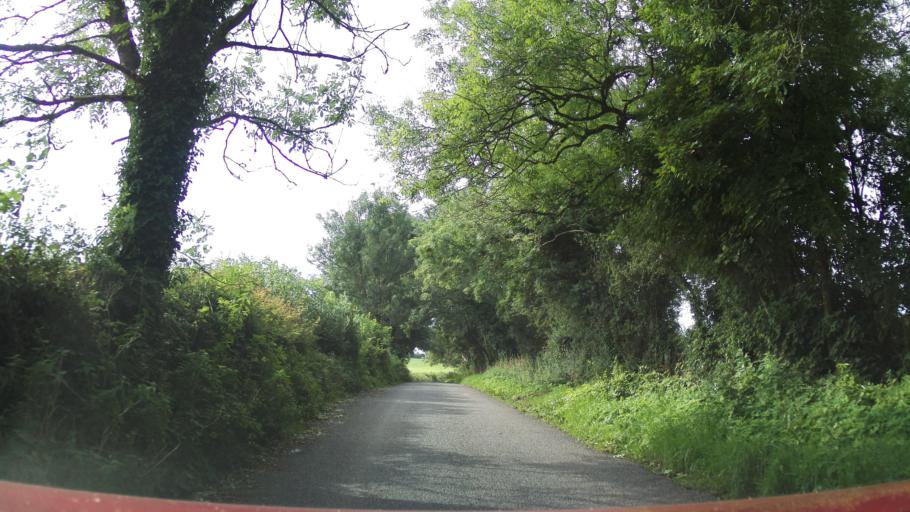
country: GB
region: England
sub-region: Somerset
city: Chilcompton
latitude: 51.2153
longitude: -2.5003
